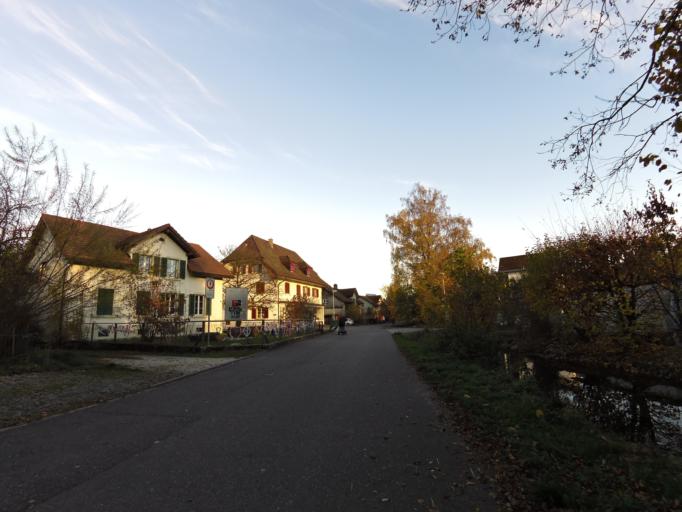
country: CH
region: Aargau
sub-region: Bezirk Aarau
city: Suhr
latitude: 47.3821
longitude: 8.0663
